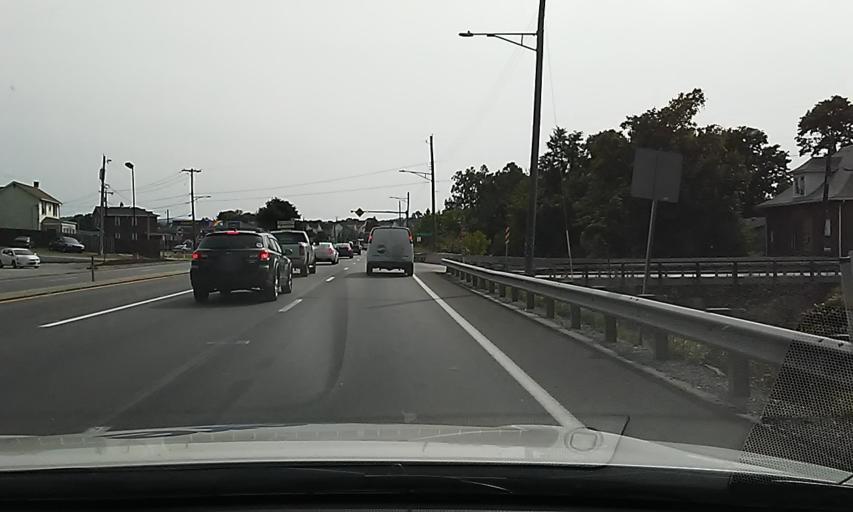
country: US
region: Pennsylvania
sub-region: Fayette County
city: Connellsville
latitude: 40.0268
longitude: -79.5893
